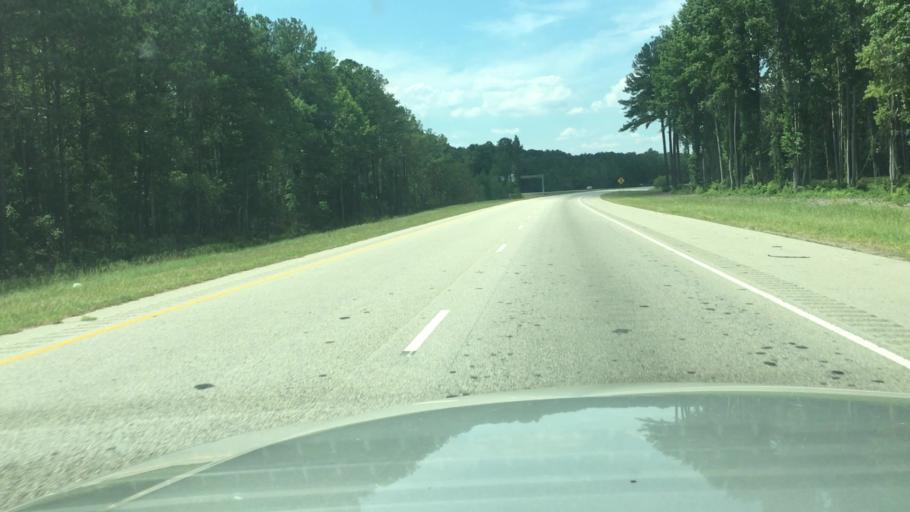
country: US
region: North Carolina
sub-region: Cumberland County
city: Fayetteville
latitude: 34.9789
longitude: -78.8576
